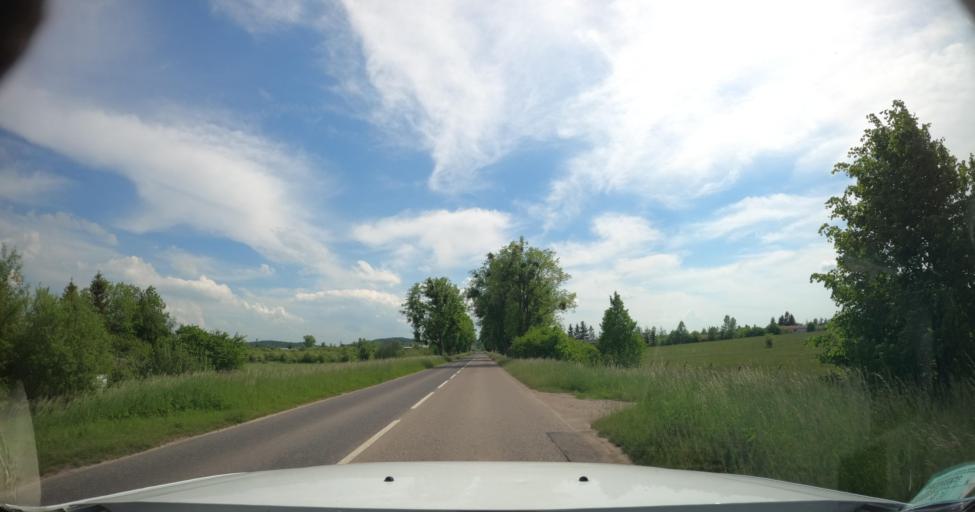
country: PL
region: Warmian-Masurian Voivodeship
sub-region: Powiat lidzbarski
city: Lidzbark Warminski
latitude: 54.1389
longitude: 20.5669
